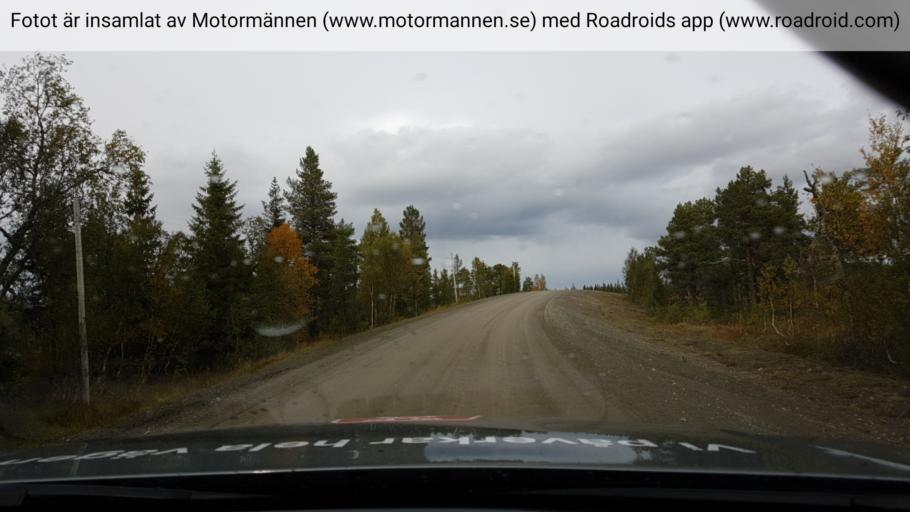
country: NO
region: Nord-Trondelag
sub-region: Snasa
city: Snaase
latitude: 63.7301
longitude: 12.4702
